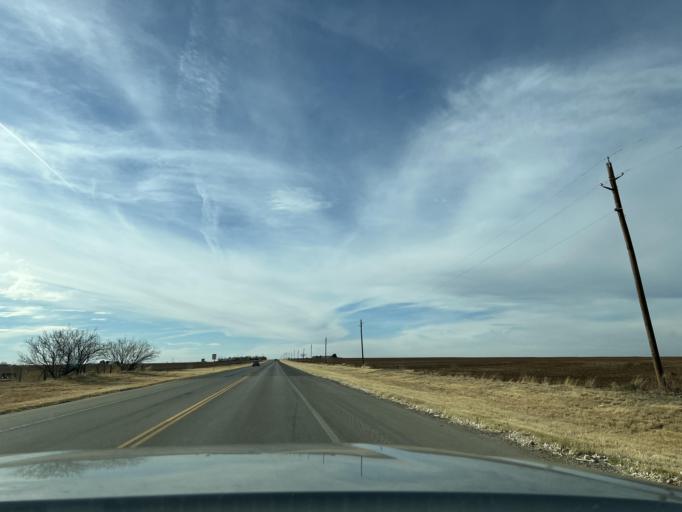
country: US
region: Texas
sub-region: Jones County
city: Anson
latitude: 32.7516
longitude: -99.9077
